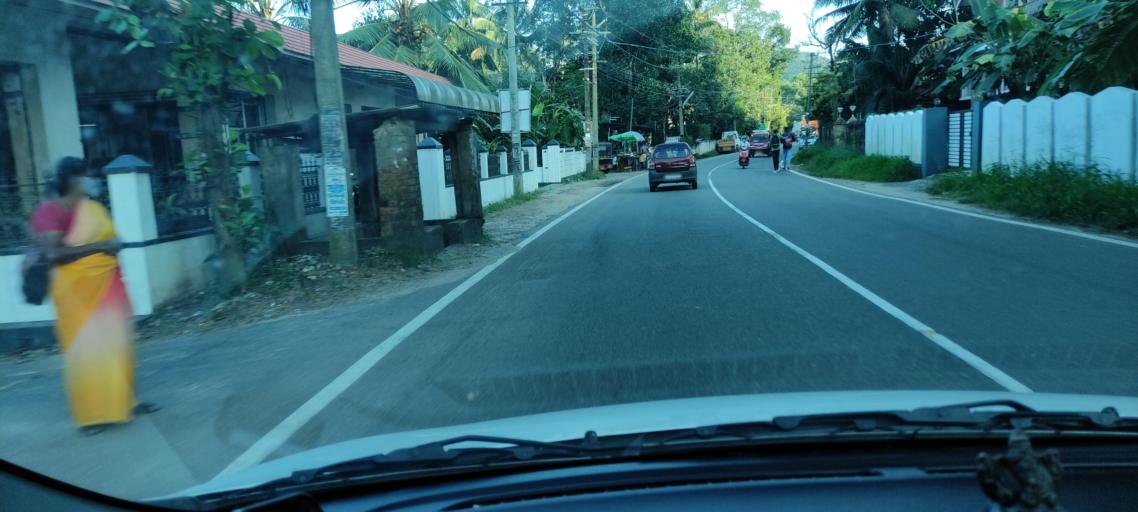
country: IN
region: Kerala
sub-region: Pattanamtitta
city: Adur
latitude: 9.1444
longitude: 76.7745
